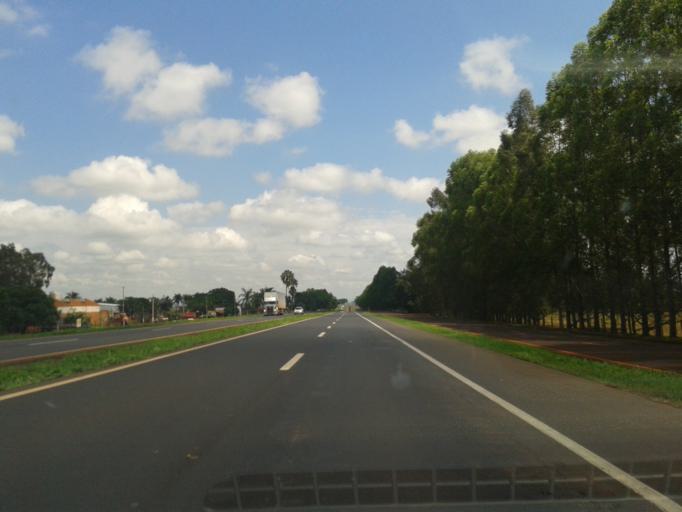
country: BR
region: Minas Gerais
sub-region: Centralina
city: Centralina
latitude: -18.5941
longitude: -49.1925
